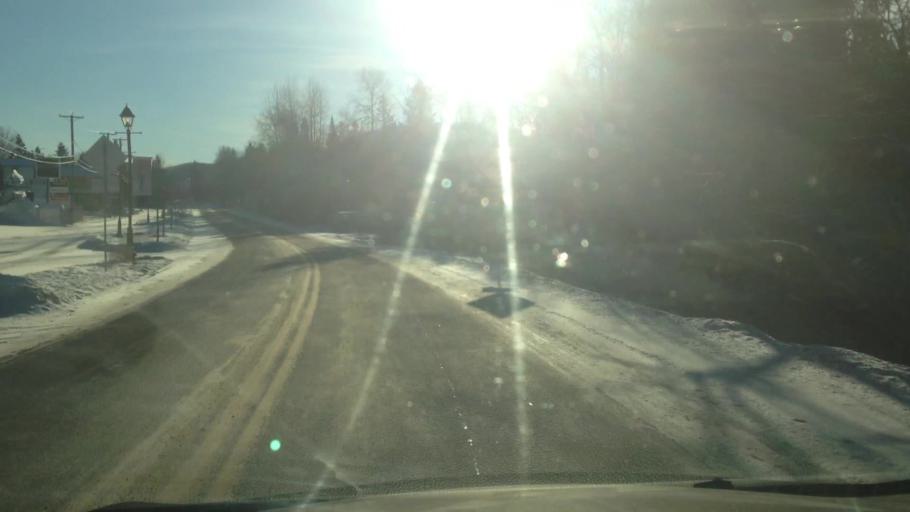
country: CA
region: Quebec
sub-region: Laurentides
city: Mont-Tremblant
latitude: 45.9454
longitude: -74.5496
